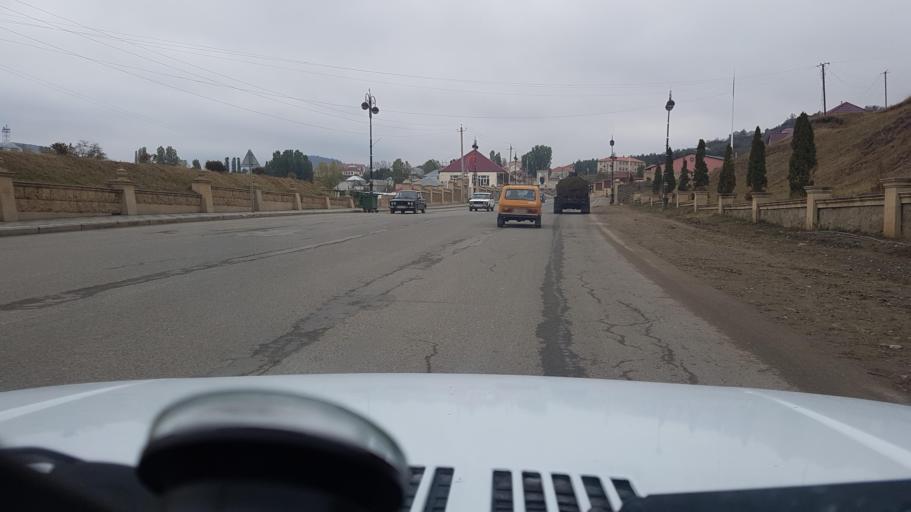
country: AZ
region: Gadabay Rayon
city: Kyadabek
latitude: 40.5839
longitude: 45.8109
